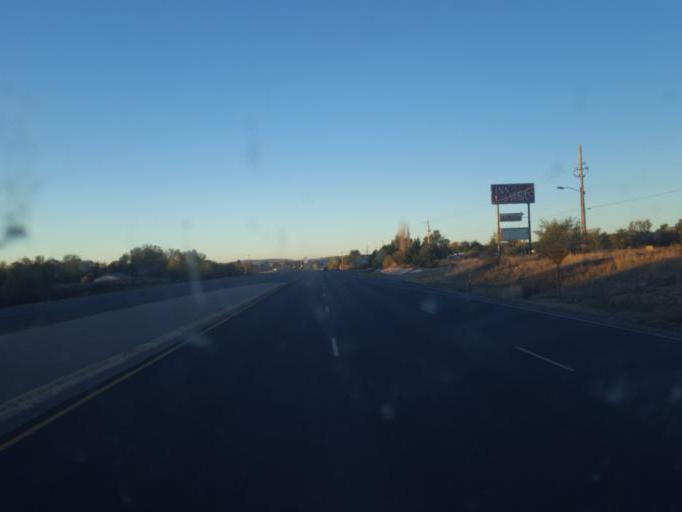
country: US
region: New Mexico
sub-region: San Miguel County
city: Las Vegas
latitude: 35.6209
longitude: -105.2066
